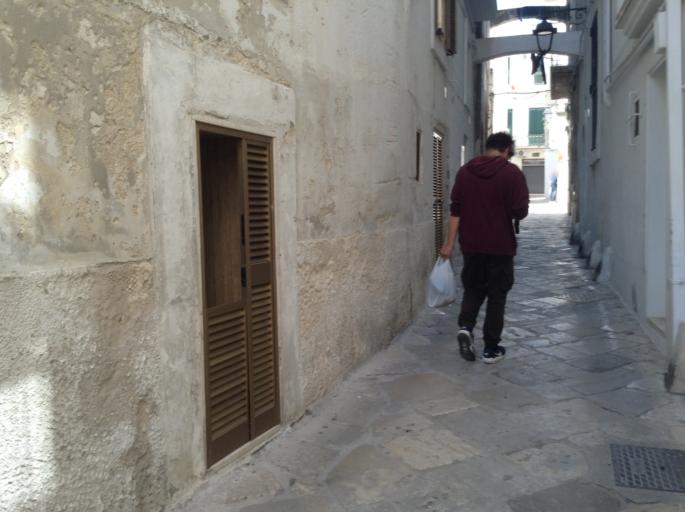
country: IT
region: Apulia
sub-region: Provincia di Bari
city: Monopoli
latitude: 40.9517
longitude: 17.3060
